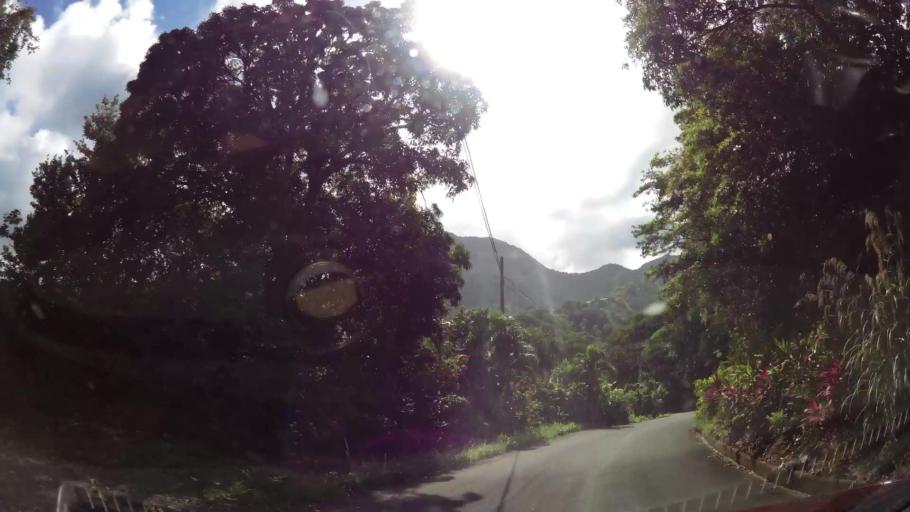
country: DM
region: Saint Andrew
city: Calibishie
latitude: 15.6170
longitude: -61.4073
